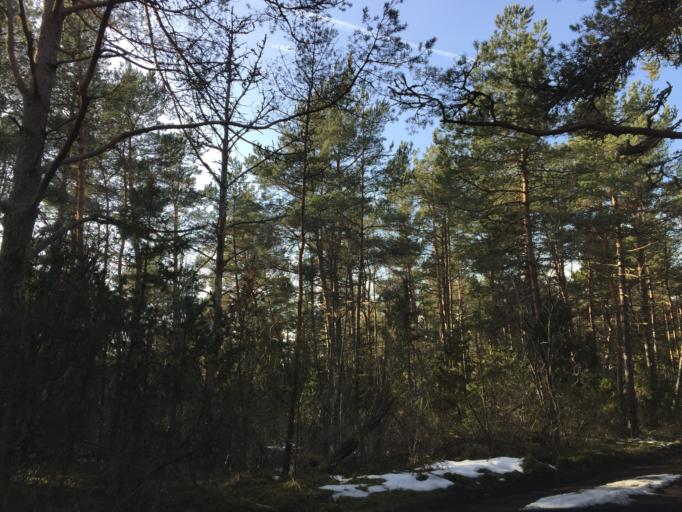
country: EE
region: Saare
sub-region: Kuressaare linn
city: Kuressaare
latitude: 58.3756
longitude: 22.0031
